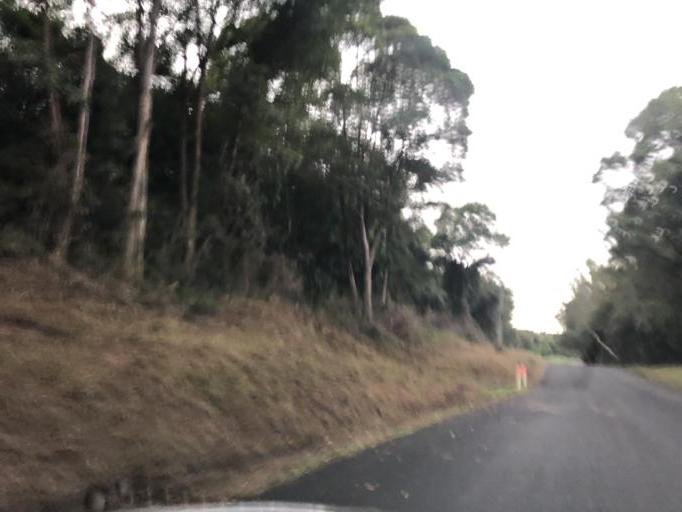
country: AU
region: New South Wales
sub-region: Coffs Harbour
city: Coffs Harbour
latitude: -30.3101
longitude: 153.1312
